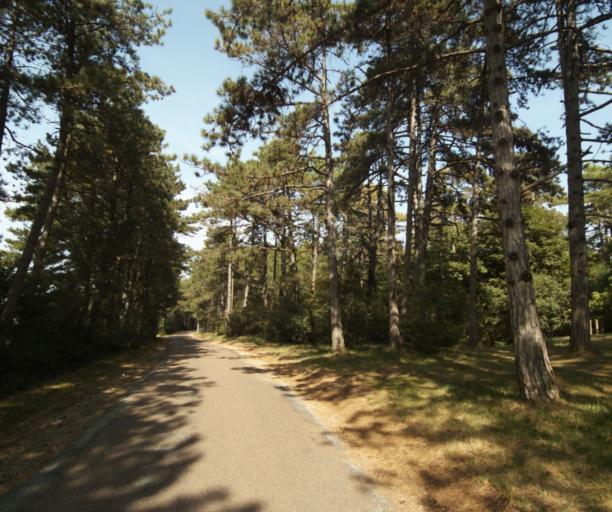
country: FR
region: Bourgogne
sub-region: Departement de Saone-et-Loire
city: Tournus
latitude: 46.5823
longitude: 4.8932
